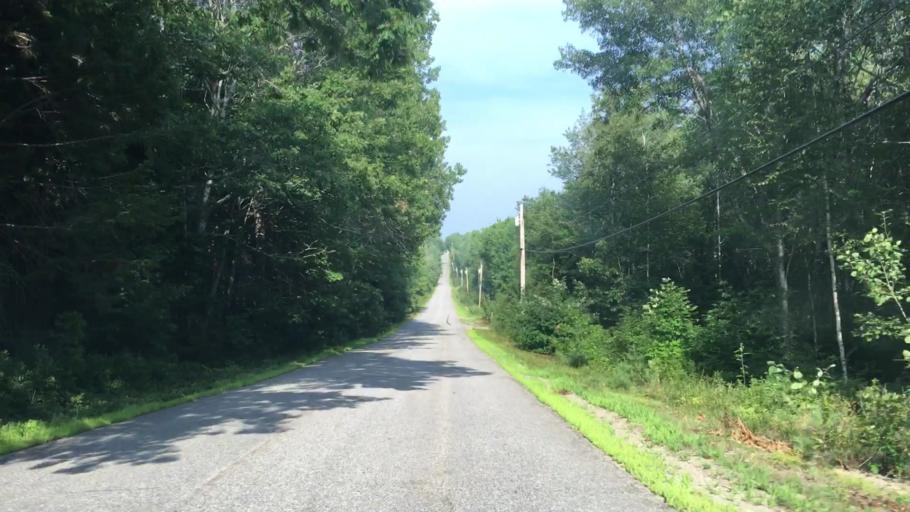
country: US
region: Maine
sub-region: Knox County
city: Friendship
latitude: 44.0340
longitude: -69.3400
